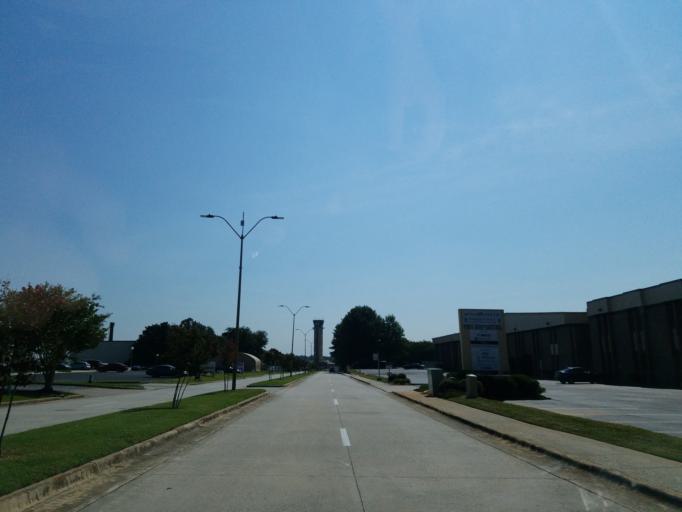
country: US
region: Georgia
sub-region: DeKalb County
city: Chamblee
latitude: 33.8764
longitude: -84.3092
